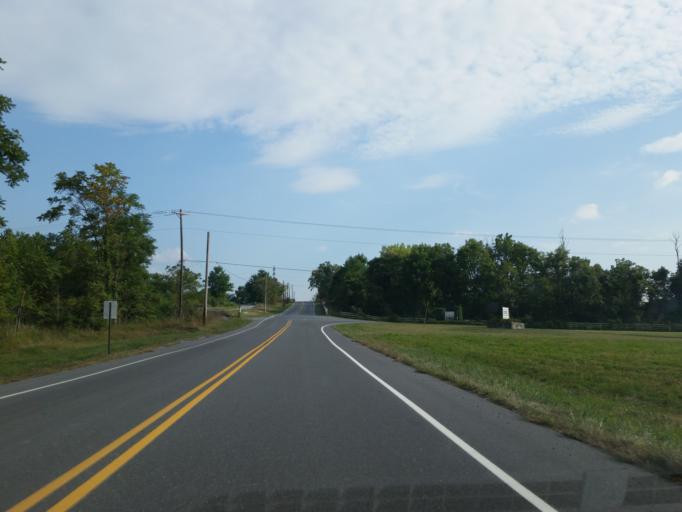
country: US
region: Pennsylvania
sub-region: Lebanon County
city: Annville
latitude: 40.3323
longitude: -76.5415
